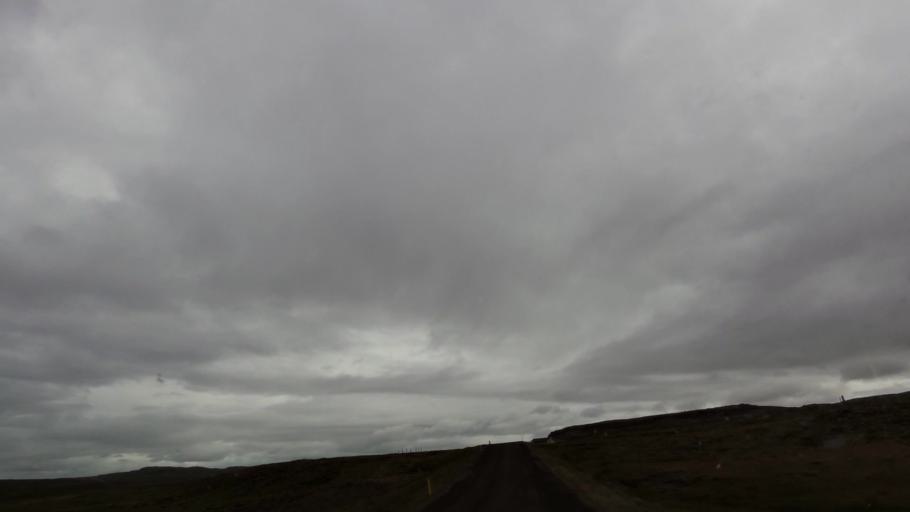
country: IS
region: West
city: Borgarnes
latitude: 65.0240
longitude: -22.1053
